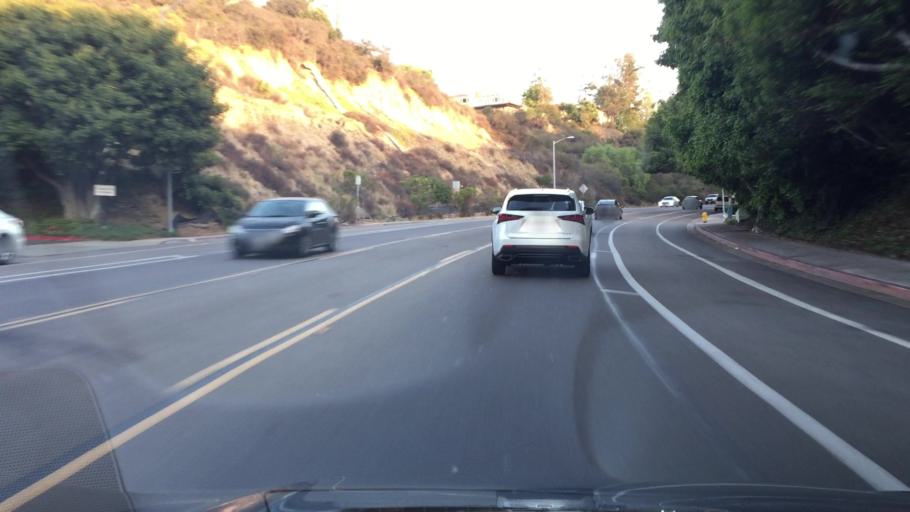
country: US
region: California
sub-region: San Diego County
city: Lemon Grove
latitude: 32.7671
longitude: -117.0840
